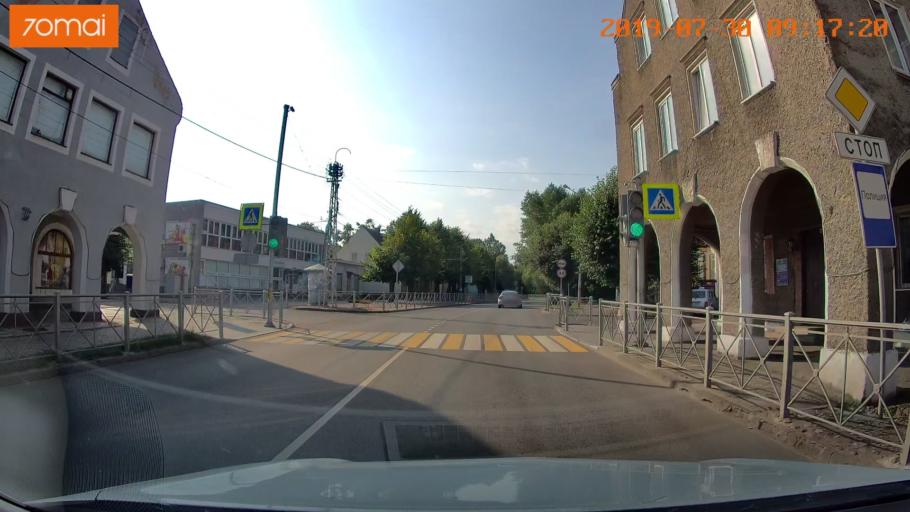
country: RU
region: Kaliningrad
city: Nesterov
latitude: 54.6343
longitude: 22.5679
